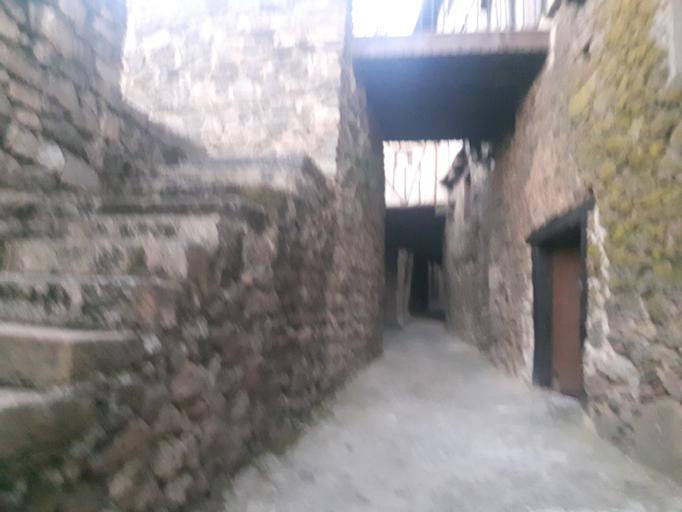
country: ES
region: Castille and Leon
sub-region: Provincia de Salamanca
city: Miranda del Castanar
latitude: 40.4854
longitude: -6.0001
